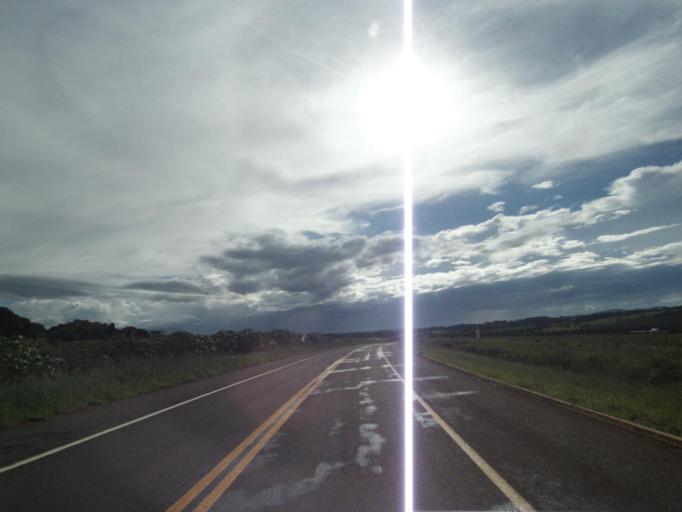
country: BR
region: Goias
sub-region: Jaragua
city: Jaragua
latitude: -15.9016
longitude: -49.5334
